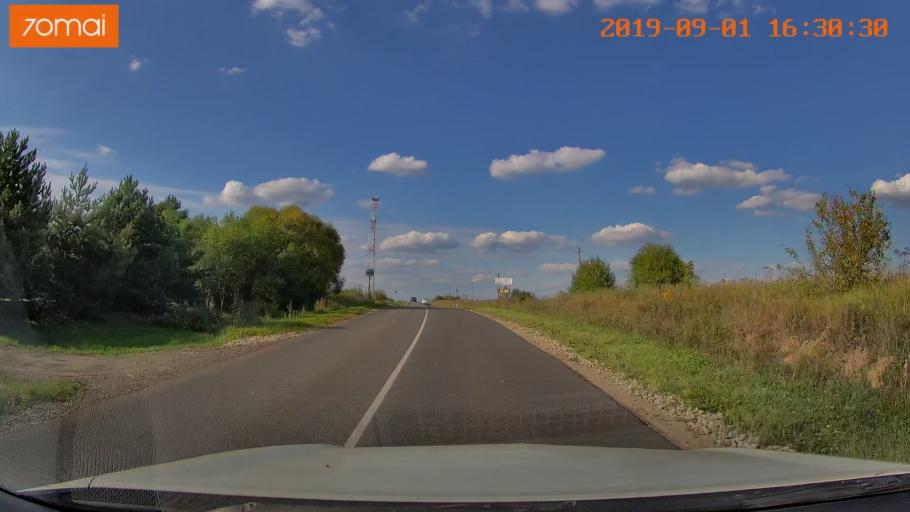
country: RU
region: Kaluga
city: Maloyaroslavets
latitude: 54.9461
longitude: 36.4588
